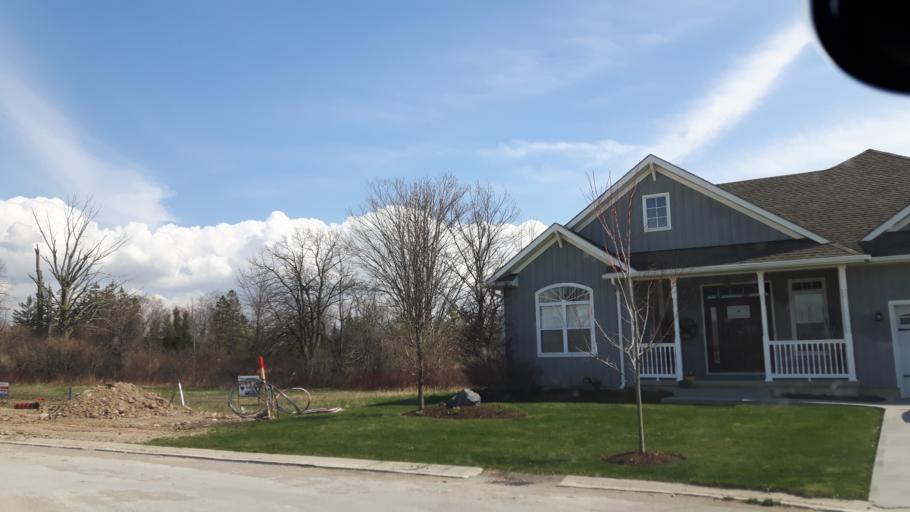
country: CA
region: Ontario
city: Bluewater
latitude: 43.5517
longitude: -81.7037
